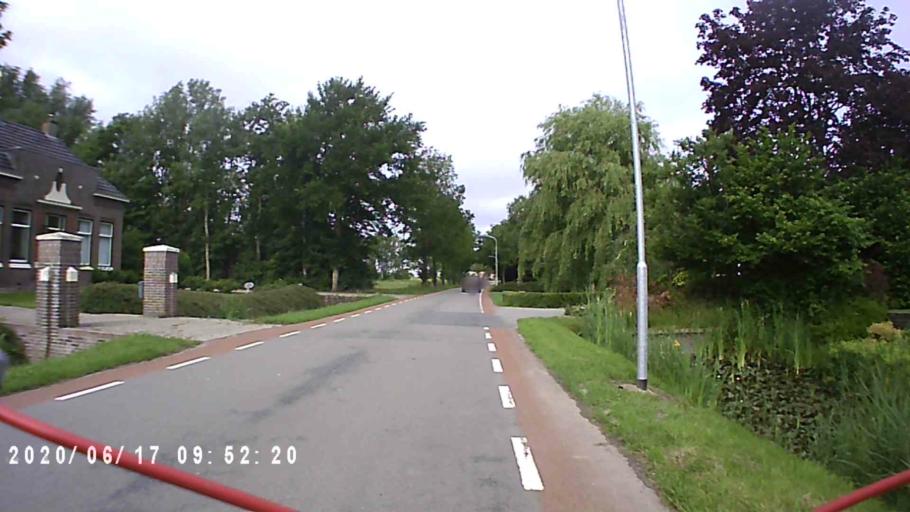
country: NL
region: Groningen
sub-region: Gemeente De Marne
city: Ulrum
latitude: 53.3596
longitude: 6.3237
